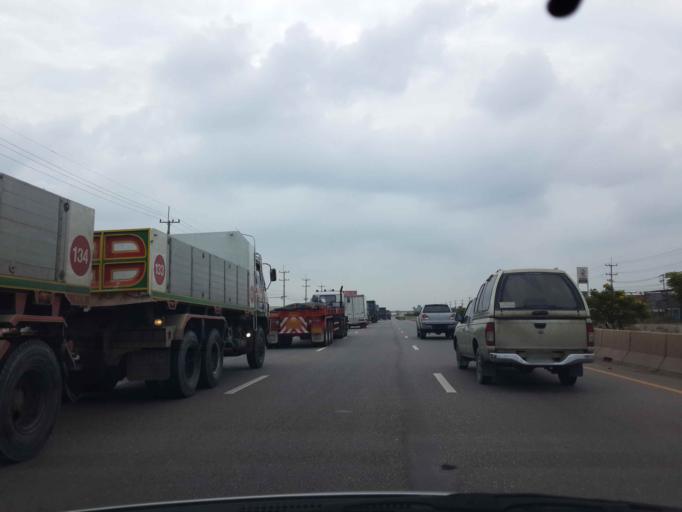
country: TH
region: Samut Sakhon
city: Ban Phaeo
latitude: 13.4724
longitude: 100.1140
